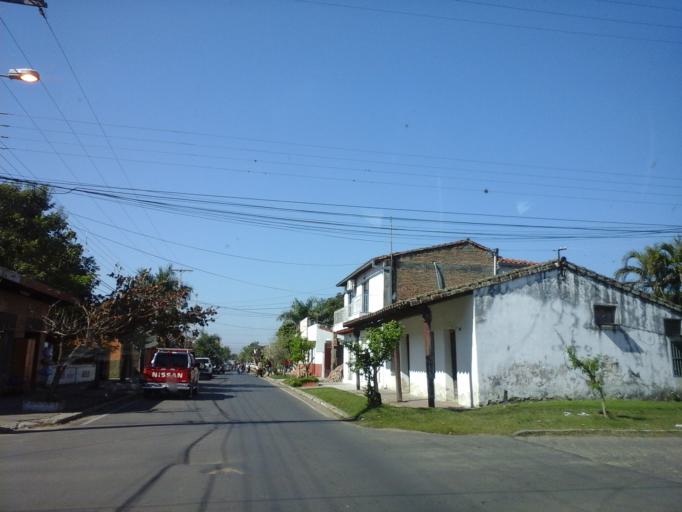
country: PY
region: Neembucu
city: Pilar
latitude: -26.8596
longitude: -58.3033
